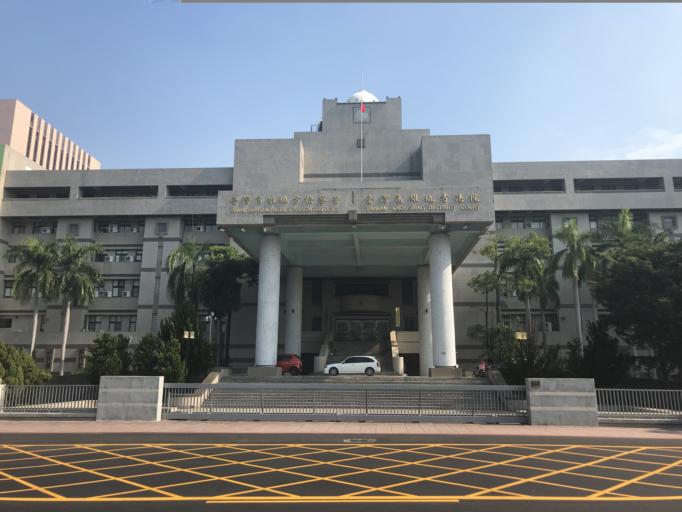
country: TW
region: Kaohsiung
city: Kaohsiung
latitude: 22.6260
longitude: 120.2893
